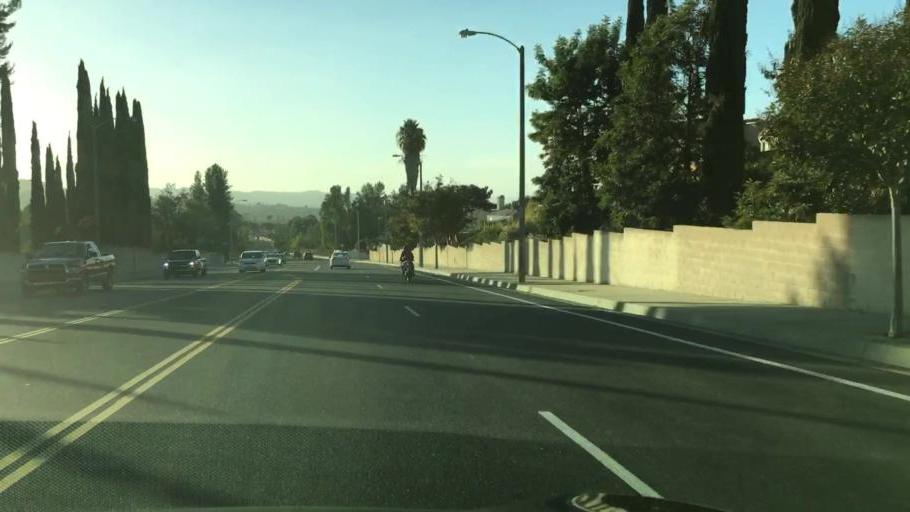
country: US
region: California
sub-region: Los Angeles County
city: Rowland Heights
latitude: 33.9740
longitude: -117.8743
